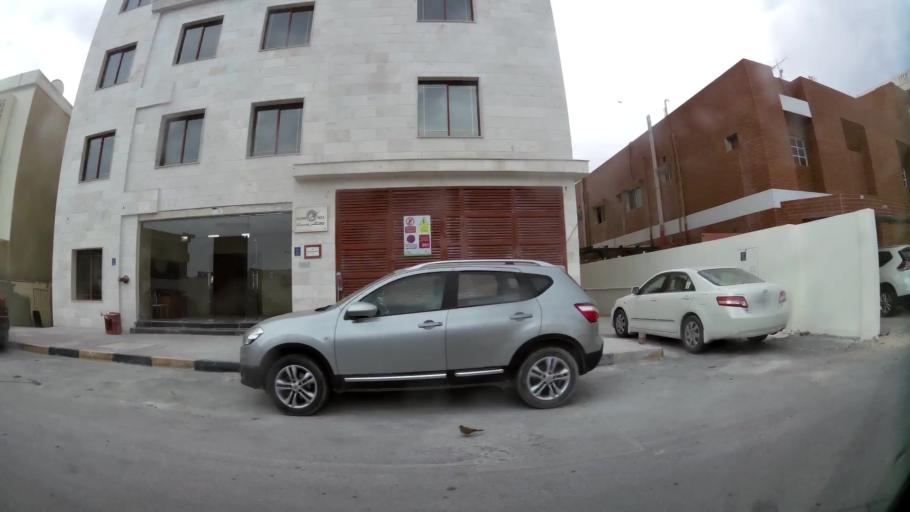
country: QA
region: Baladiyat ad Dawhah
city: Doha
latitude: 25.2744
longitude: 51.5044
